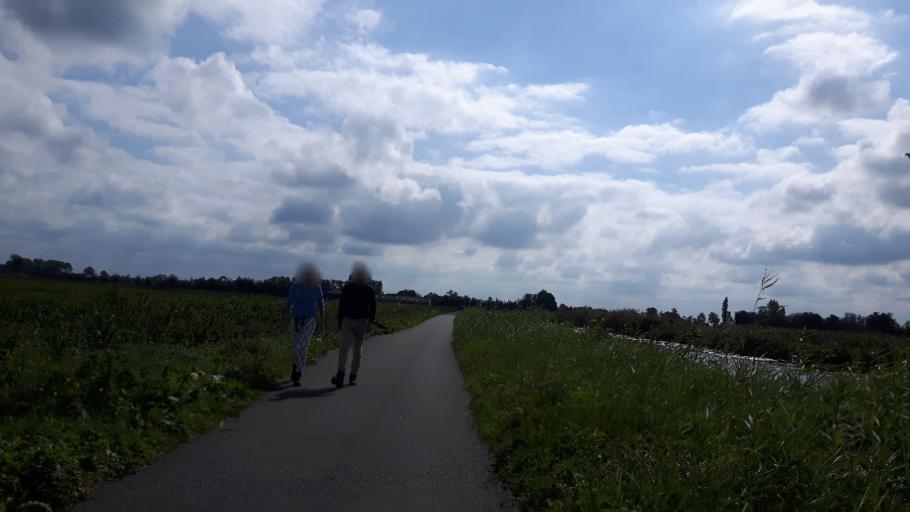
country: NL
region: South Holland
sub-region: Gemeente Nieuwkoop
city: Nieuwkoop
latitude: 52.1481
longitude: 4.8310
